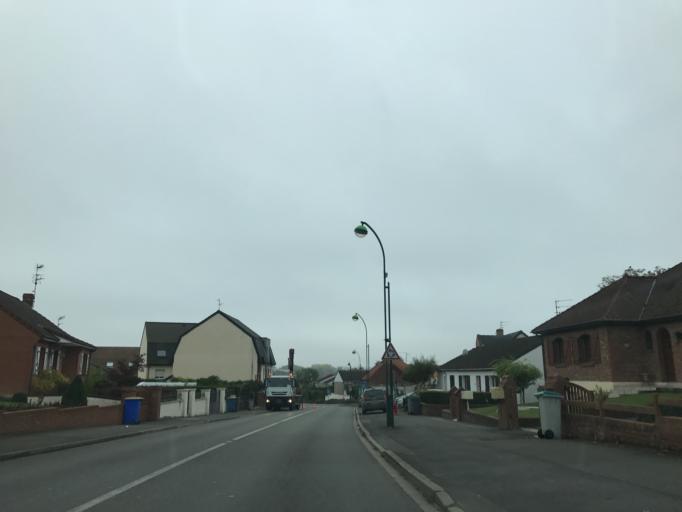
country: FR
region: Nord-Pas-de-Calais
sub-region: Departement du Pas-de-Calais
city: Saint-Laurent-Blangy
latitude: 50.3042
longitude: 2.8016
